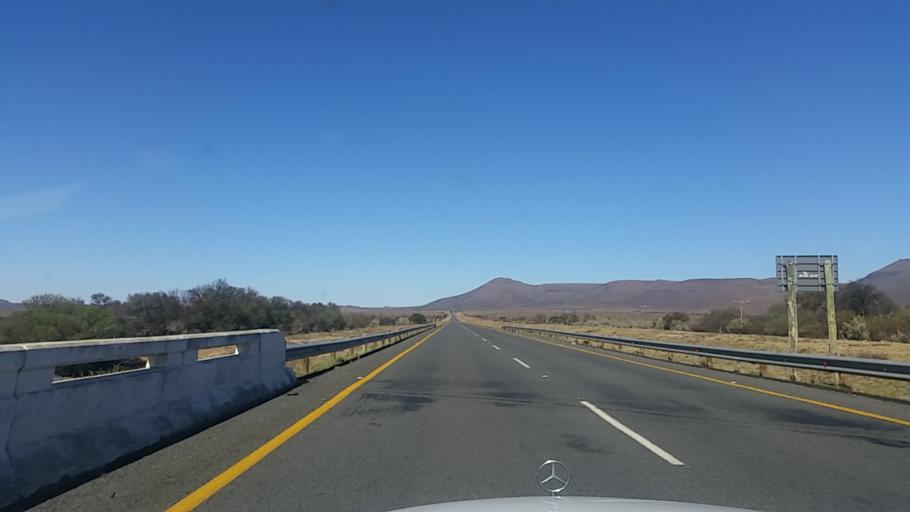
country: ZA
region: Eastern Cape
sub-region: Cacadu District Municipality
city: Graaff-Reinet
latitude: -32.0056
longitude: 24.6597
